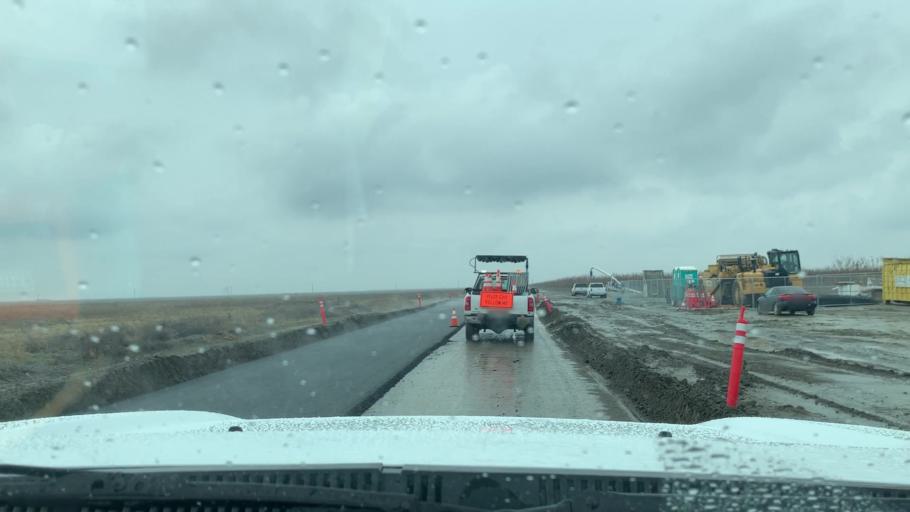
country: US
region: California
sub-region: Kings County
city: Corcoran
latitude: 36.0073
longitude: -119.4971
